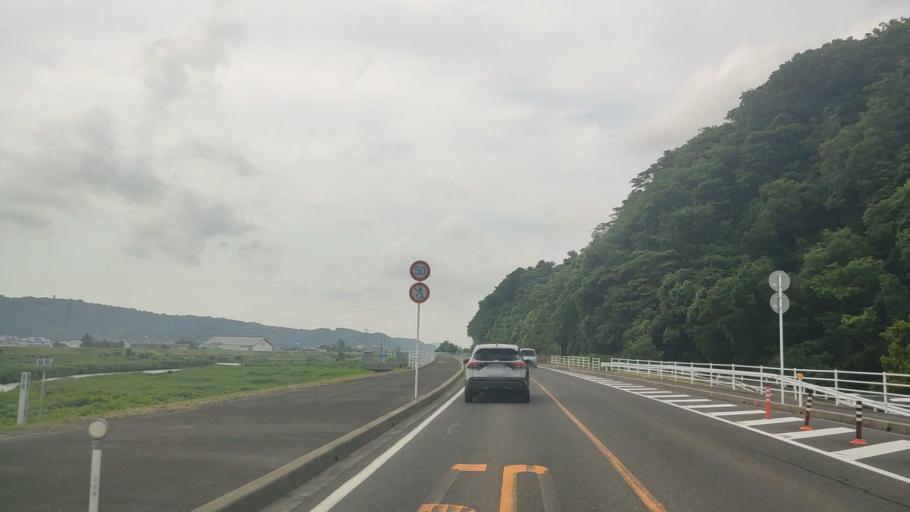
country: JP
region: Tottori
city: Kurayoshi
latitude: 35.4302
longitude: 133.8496
